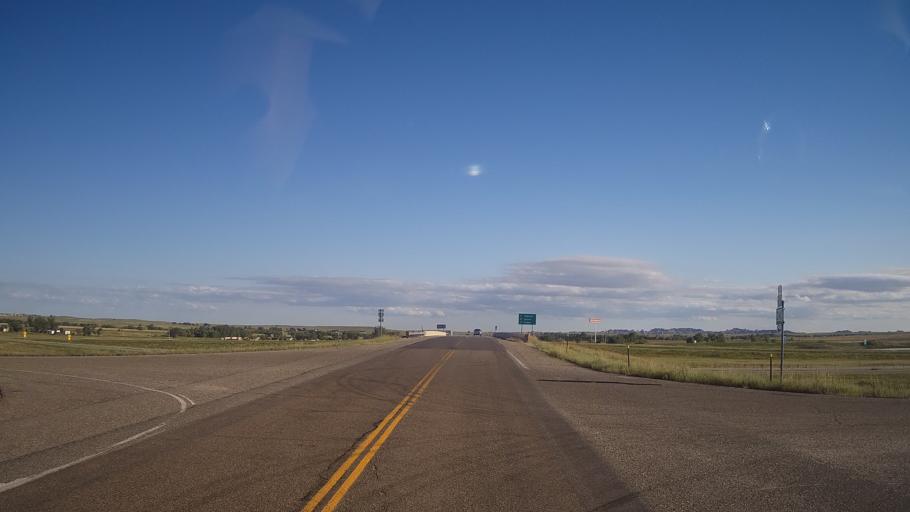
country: US
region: South Dakota
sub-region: Haakon County
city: Philip
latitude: 43.8416
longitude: -101.9022
